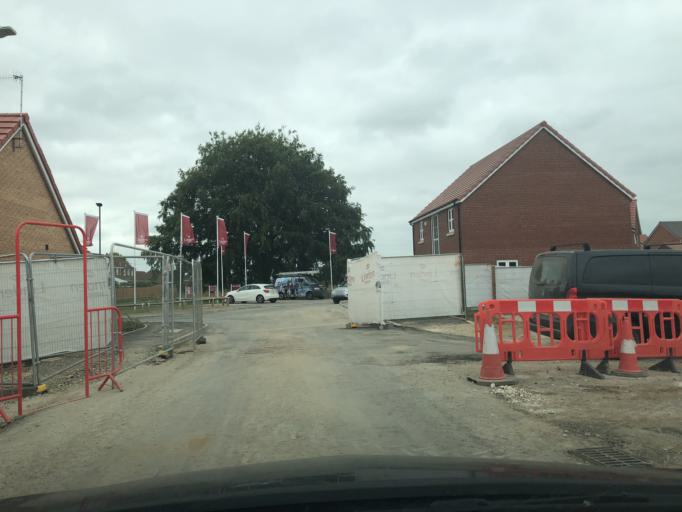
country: GB
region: England
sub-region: North Yorkshire
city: East Ayton
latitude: 54.2435
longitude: -0.4890
